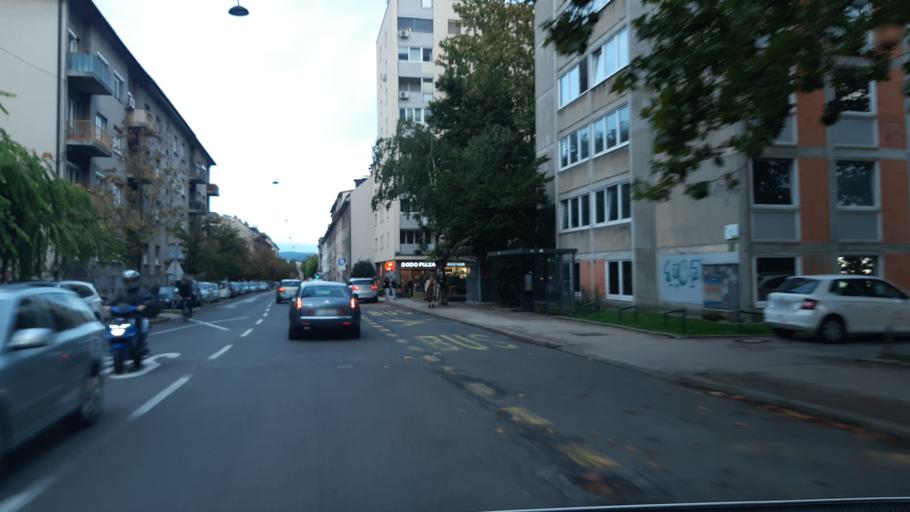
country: SI
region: Ljubljana
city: Ljubljana
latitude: 46.0531
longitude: 14.5134
